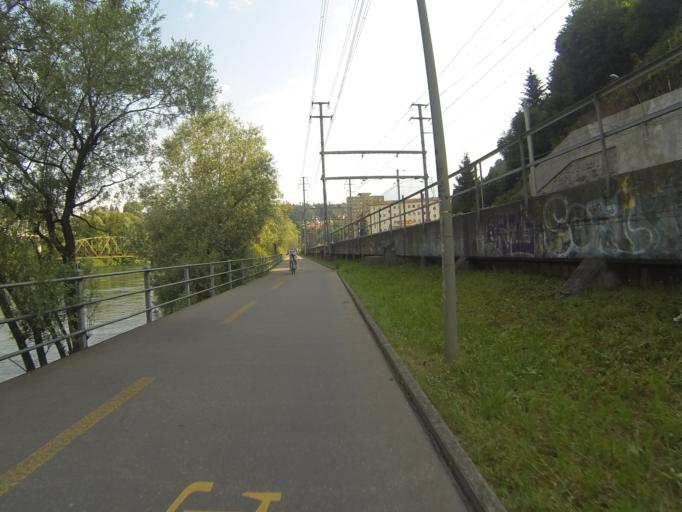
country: CH
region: Lucerne
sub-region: Hochdorf District
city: Emmen
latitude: 47.0611
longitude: 8.2862
